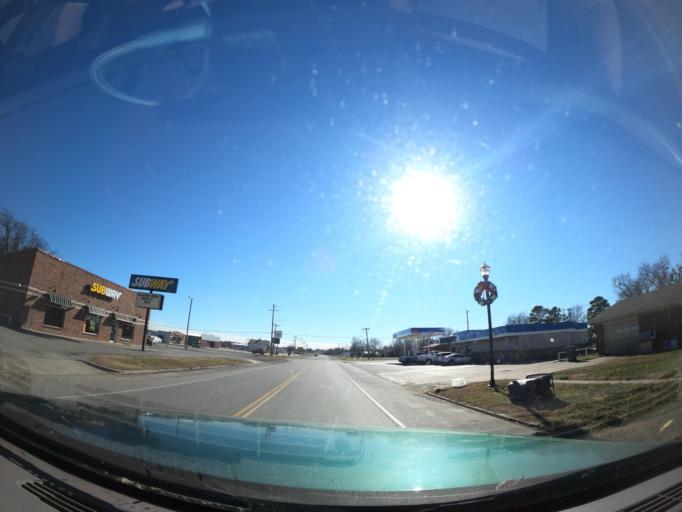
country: US
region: Oklahoma
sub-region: Muskogee County
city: Haskell
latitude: 35.8138
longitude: -95.6750
